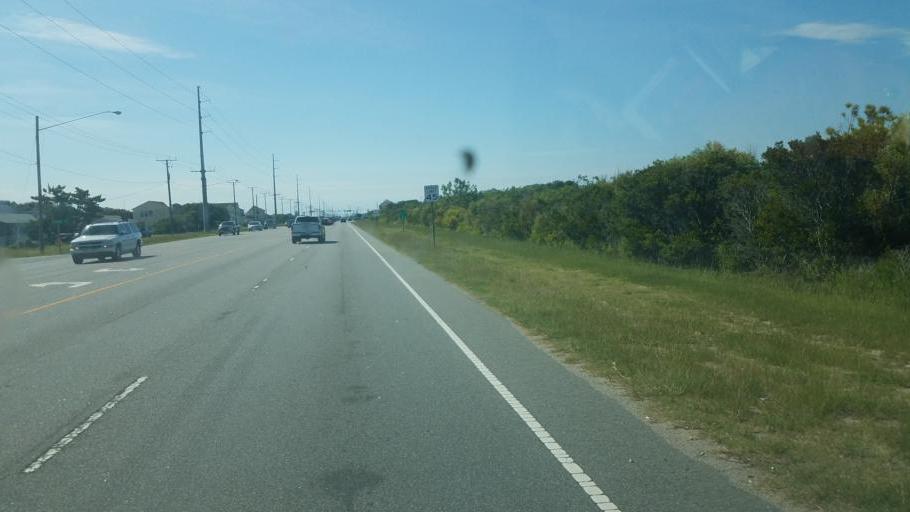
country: US
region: North Carolina
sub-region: Dare County
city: Kill Devil Hills
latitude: 36.0171
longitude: -75.6631
